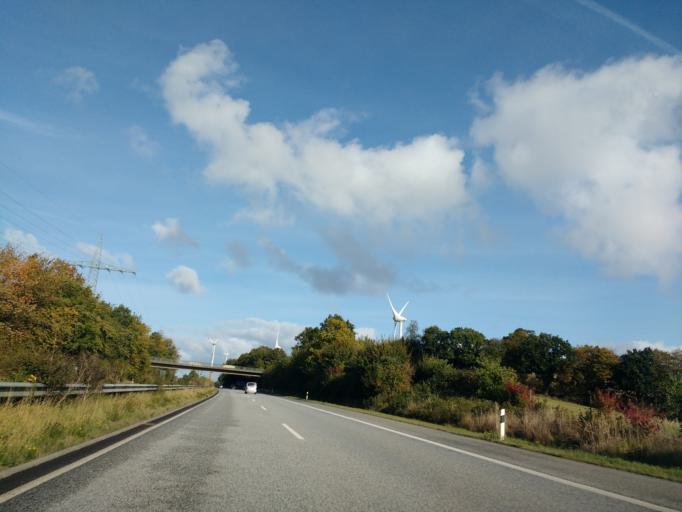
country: DE
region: Schleswig-Holstein
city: Kabelhorst
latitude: 54.2195
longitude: 10.9023
